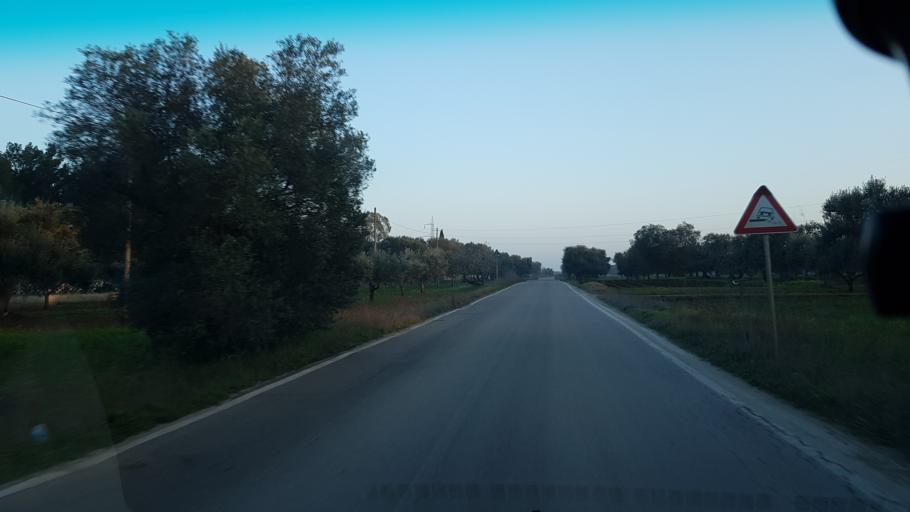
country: IT
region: Apulia
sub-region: Provincia di Brindisi
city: San Vito dei Normanni
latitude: 40.6405
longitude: 17.7791
